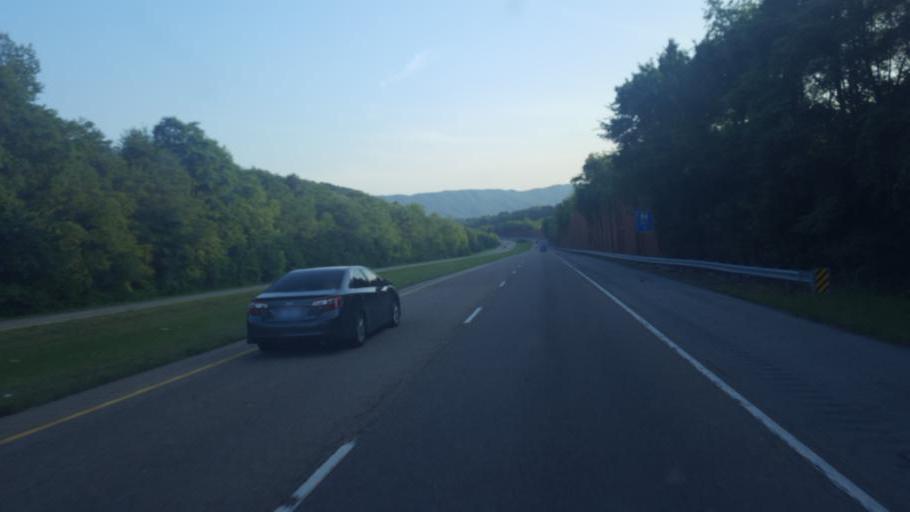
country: US
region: Tennessee
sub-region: Sullivan County
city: Kingsport
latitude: 36.5734
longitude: -82.5817
